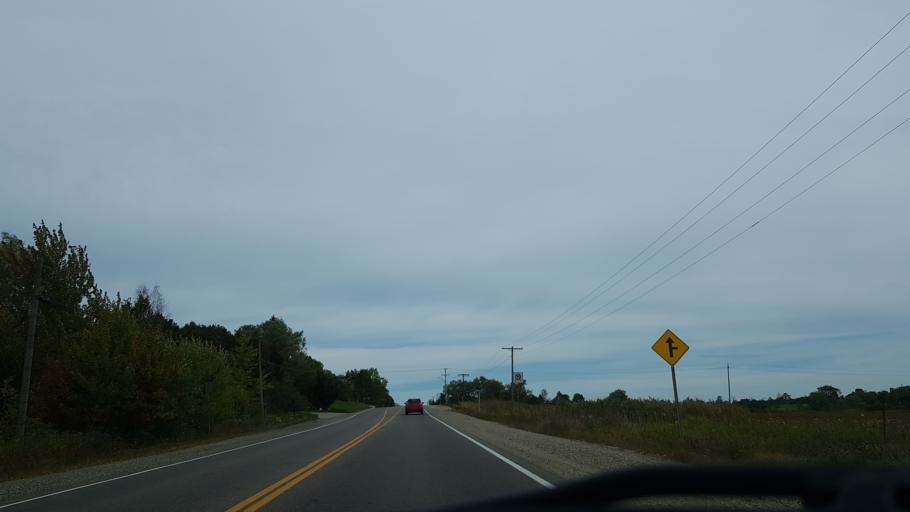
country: CA
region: Ontario
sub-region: Wellington County
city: Guelph
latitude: 43.5888
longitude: -80.2429
